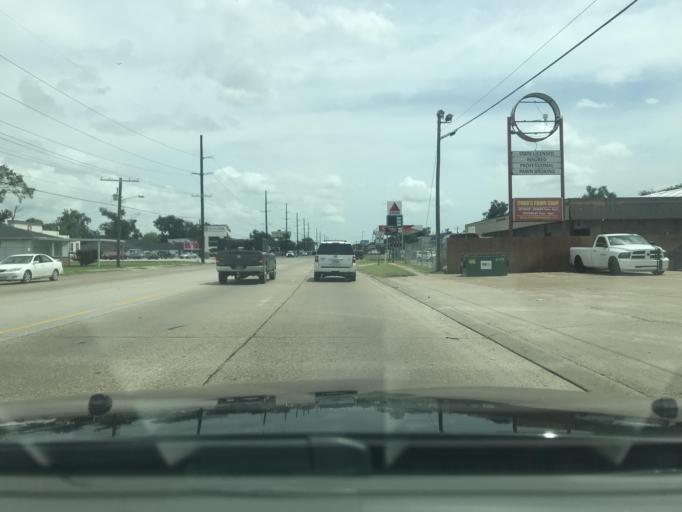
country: US
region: Louisiana
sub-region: Calcasieu Parish
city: Lake Charles
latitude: 30.2162
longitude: -93.1802
